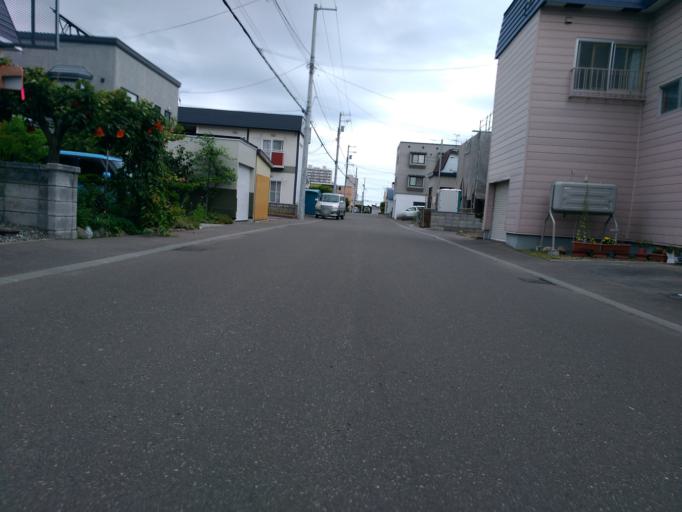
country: JP
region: Hokkaido
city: Ebetsu
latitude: 43.0852
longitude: 141.5270
